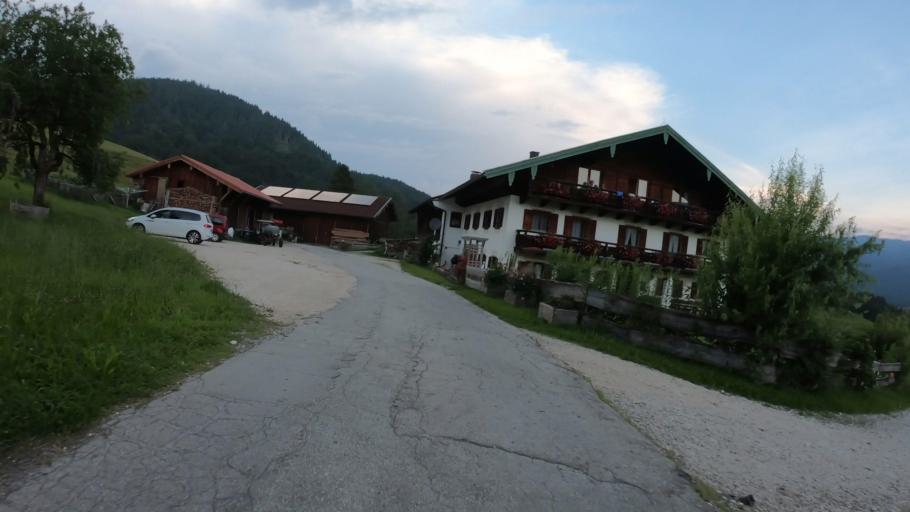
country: DE
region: Bavaria
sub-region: Upper Bavaria
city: Inzell
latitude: 47.7647
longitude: 12.7234
